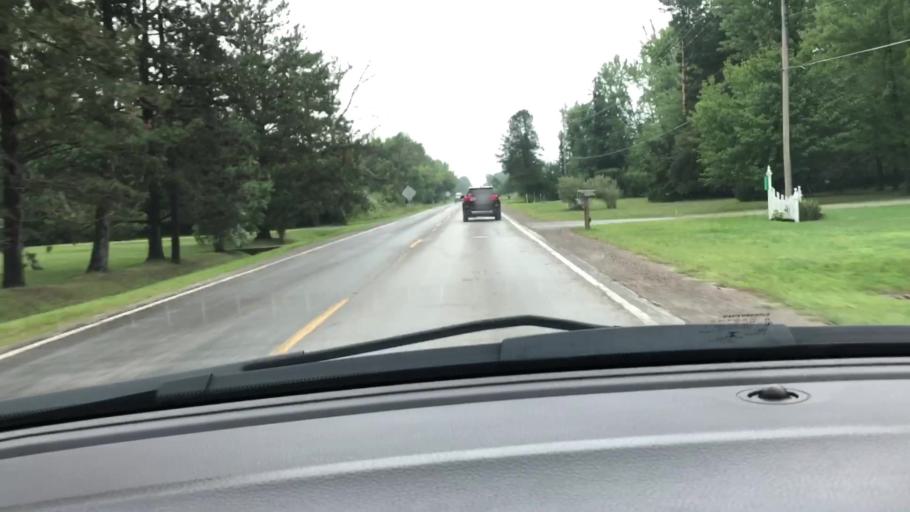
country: US
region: Michigan
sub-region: Saginaw County
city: Freeland
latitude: 43.4895
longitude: -84.0913
